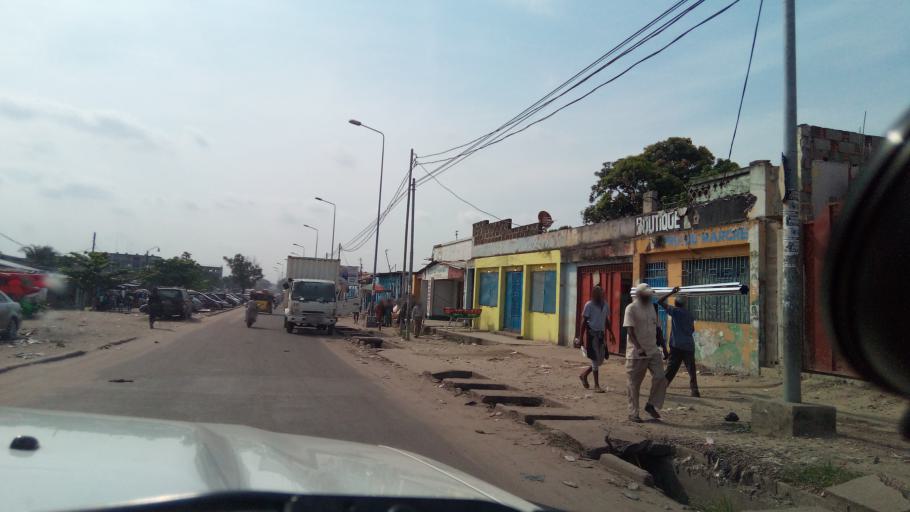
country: CD
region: Kinshasa
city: Kinshasa
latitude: -4.3475
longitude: 15.3140
